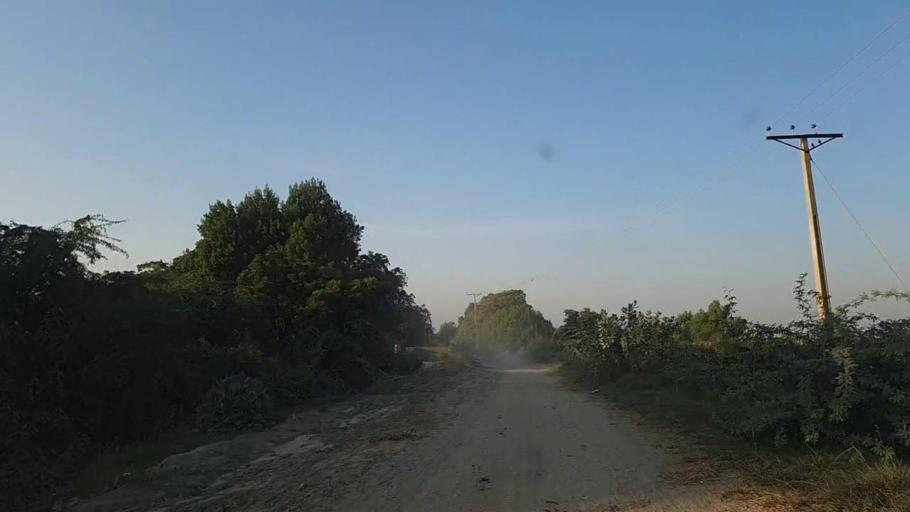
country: PK
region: Sindh
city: Mirpur Batoro
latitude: 24.7227
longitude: 68.2138
